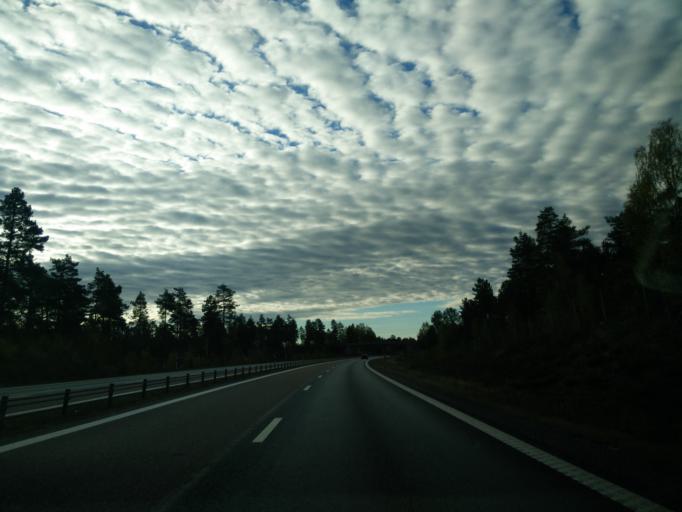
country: SE
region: Gaevleborg
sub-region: Soderhamns Kommun
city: Soderhamn
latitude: 61.3175
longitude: 17.0348
